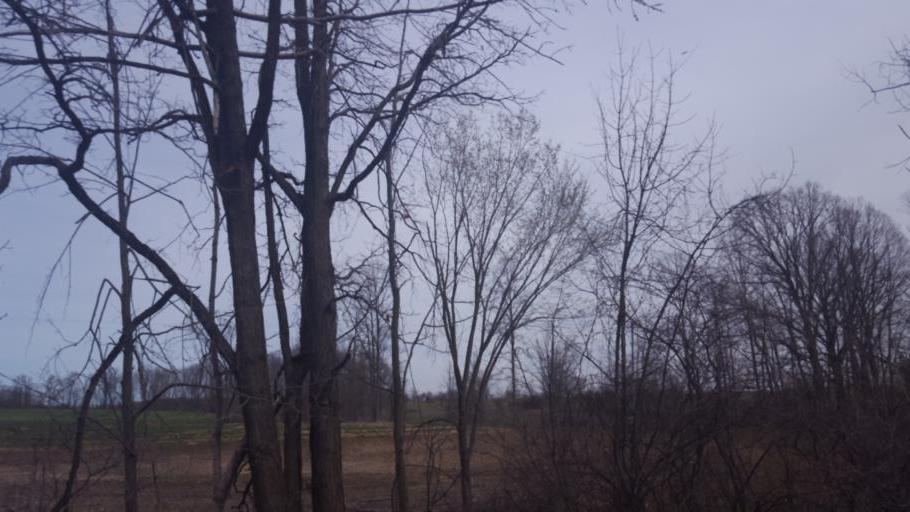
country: US
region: Michigan
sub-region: Midland County
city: Coleman
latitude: 43.8773
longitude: -84.6463
